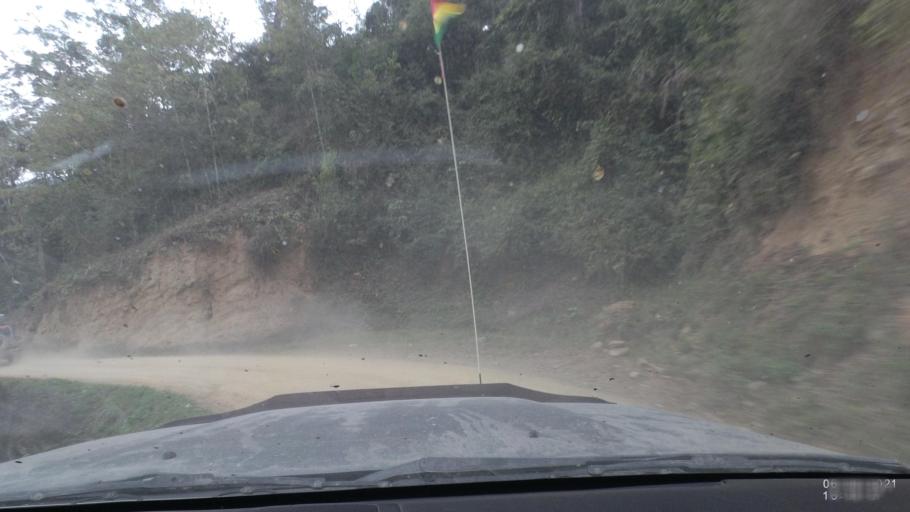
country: BO
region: La Paz
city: Quime
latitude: -16.5194
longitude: -66.7699
